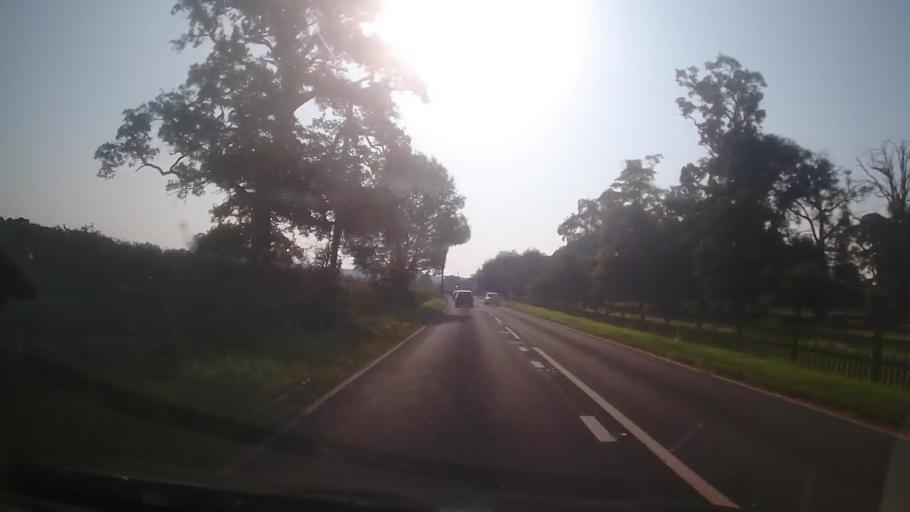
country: GB
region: England
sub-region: Shropshire
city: Alveley
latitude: 52.4986
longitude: -2.3709
